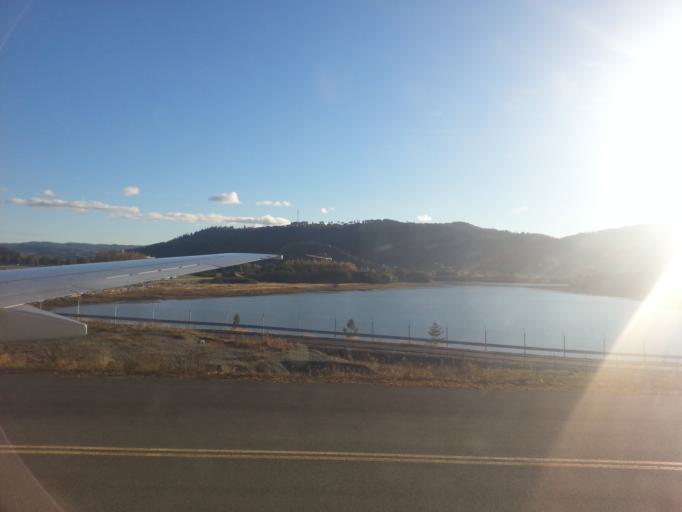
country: NO
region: Nord-Trondelag
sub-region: Stjordal
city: Stjordal
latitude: 63.4559
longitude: 10.9075
